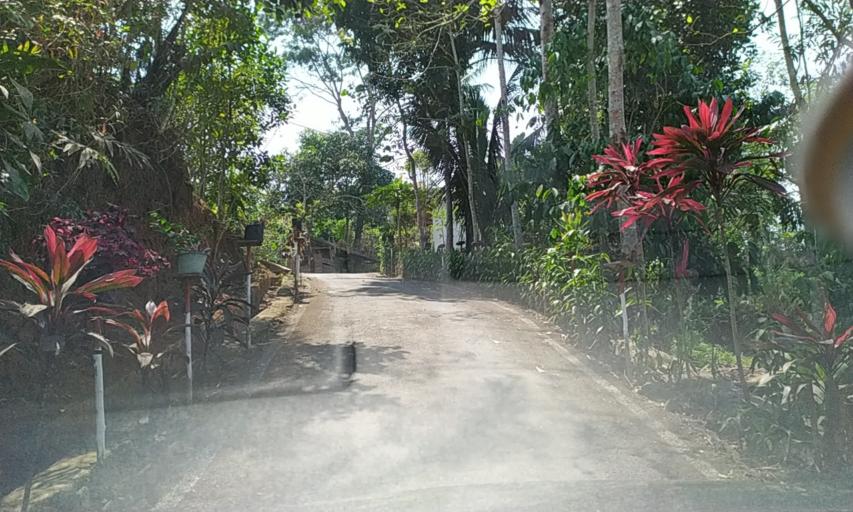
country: ID
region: Central Java
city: Cilumping
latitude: -7.1873
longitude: 108.6211
